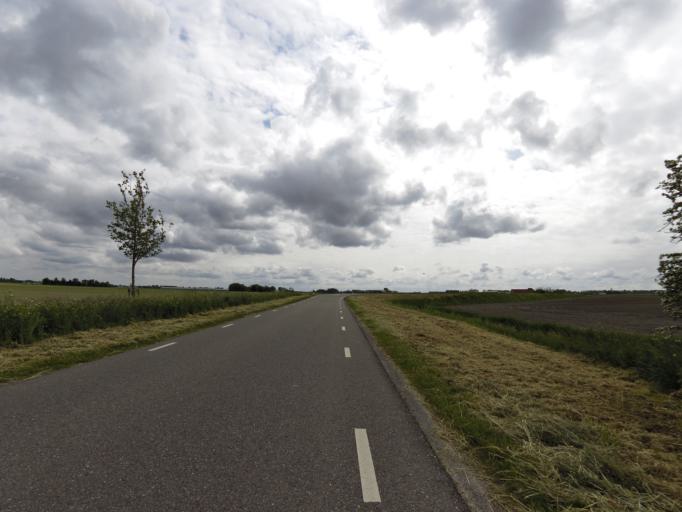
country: NL
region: South Holland
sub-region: Gemeente Hellevoetsluis
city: Nieuwenhoorn
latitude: 51.8789
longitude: 4.1335
